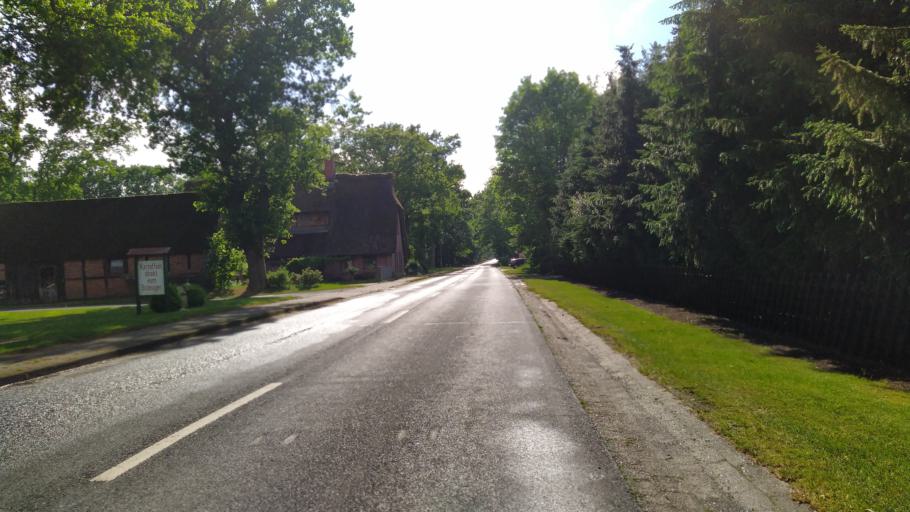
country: DE
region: Lower Saxony
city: Brest
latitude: 53.4516
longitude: 9.3894
